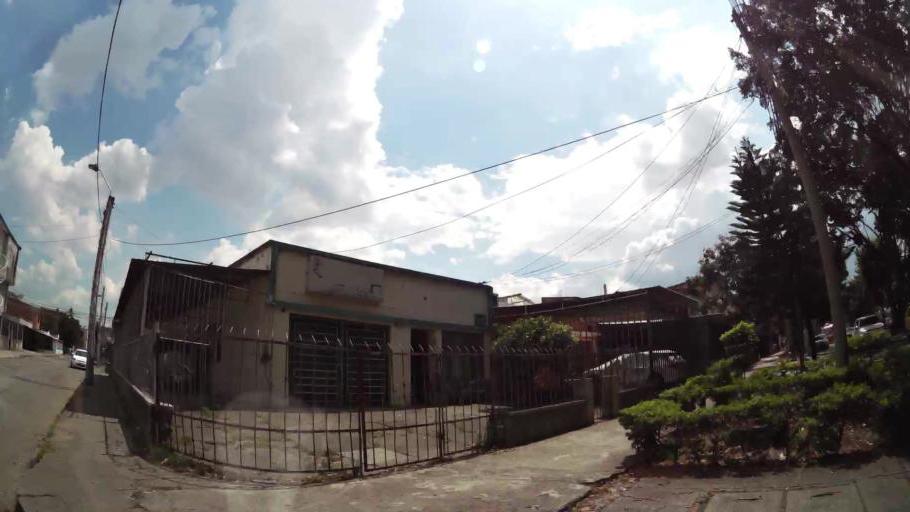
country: CO
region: Valle del Cauca
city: Cali
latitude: 3.4677
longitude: -76.5031
